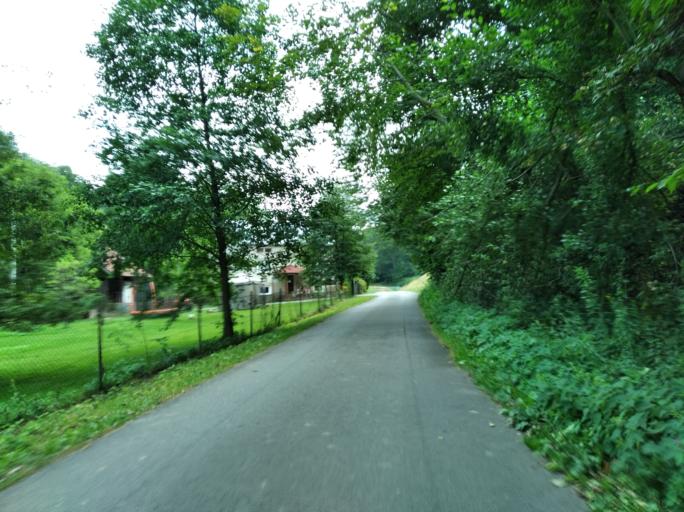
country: PL
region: Subcarpathian Voivodeship
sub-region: Powiat krosnienski
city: Wojaszowka
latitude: 49.7835
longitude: 21.7038
